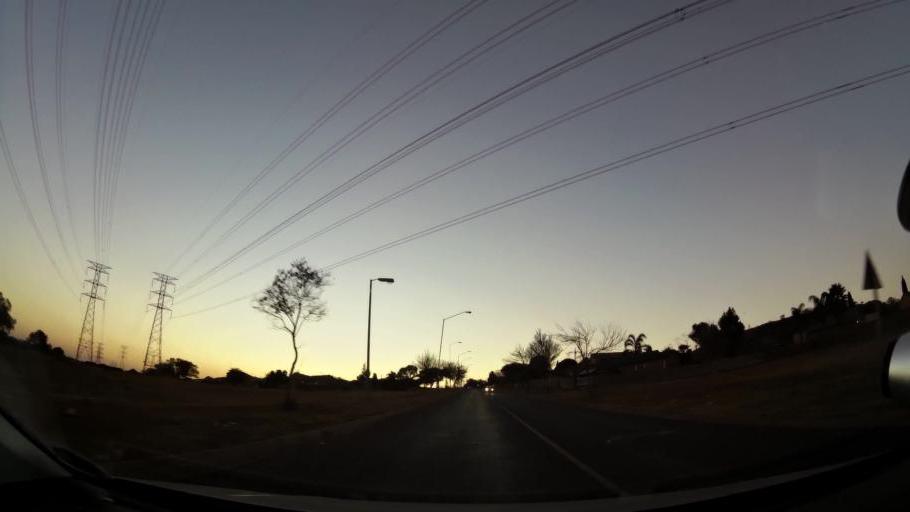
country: ZA
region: Gauteng
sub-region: City of Tshwane Metropolitan Municipality
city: Pretoria
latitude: -25.7338
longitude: 28.1423
